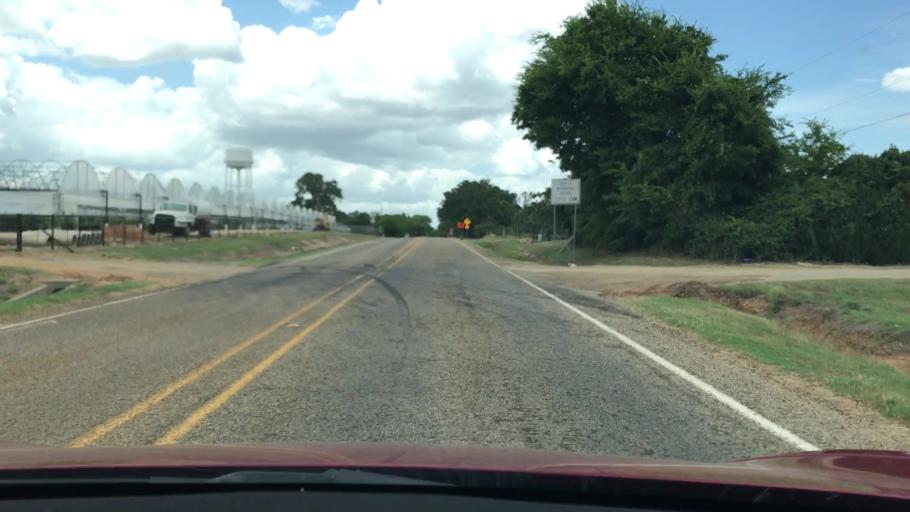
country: US
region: Texas
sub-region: Smith County
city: Hideaway
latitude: 32.4763
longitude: -95.4455
